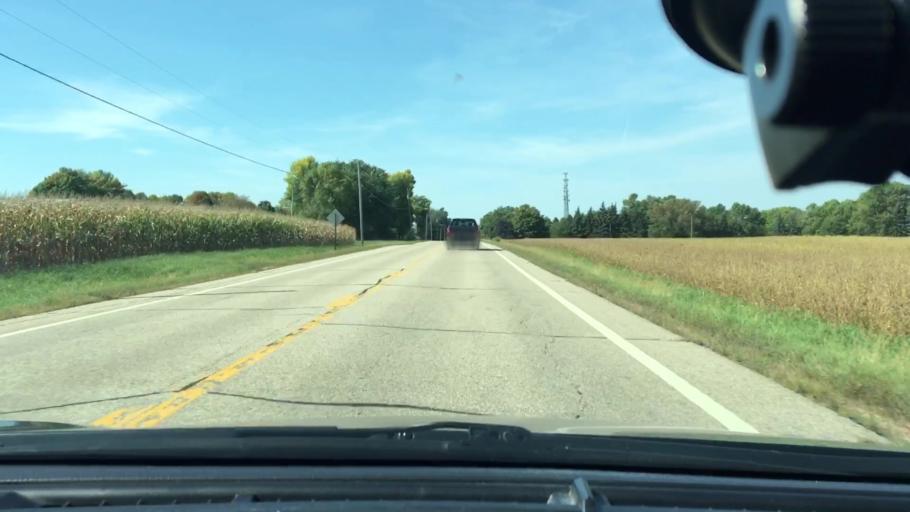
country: US
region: Minnesota
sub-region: Wright County
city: Hanover
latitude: 45.1237
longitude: -93.6219
